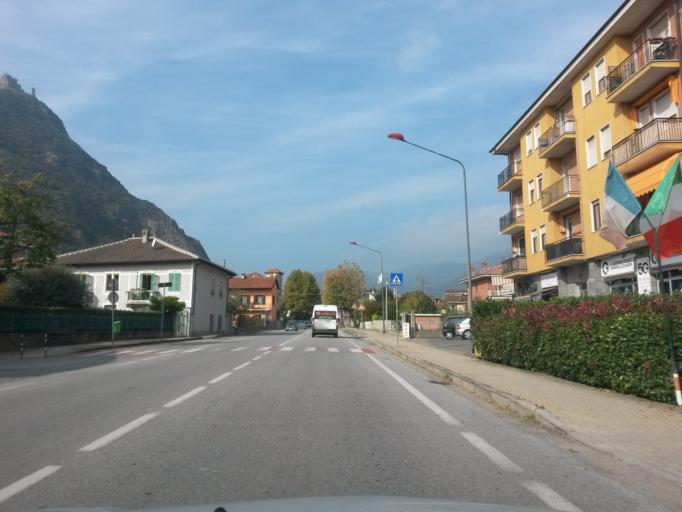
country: IT
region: Piedmont
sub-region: Provincia di Torino
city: Sant'Ambrogio di Torino
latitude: 45.0998
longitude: 7.3631
